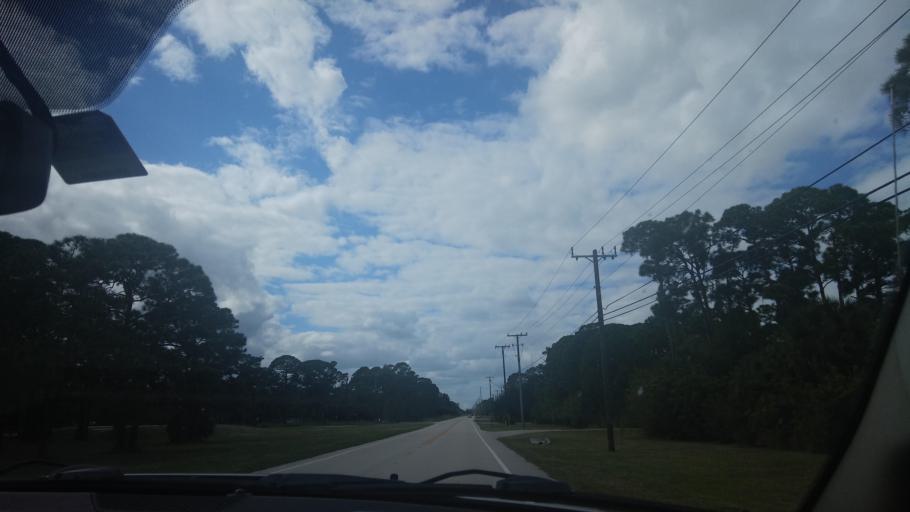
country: US
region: Florida
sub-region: Indian River County
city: Winter Beach
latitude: 27.7338
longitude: -80.4397
